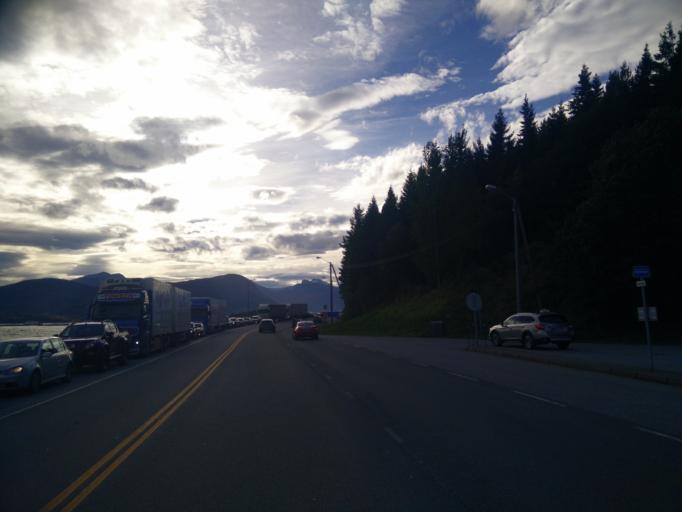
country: NO
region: More og Romsdal
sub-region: Vestnes
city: Vestnes
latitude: 62.6517
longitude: 7.0851
